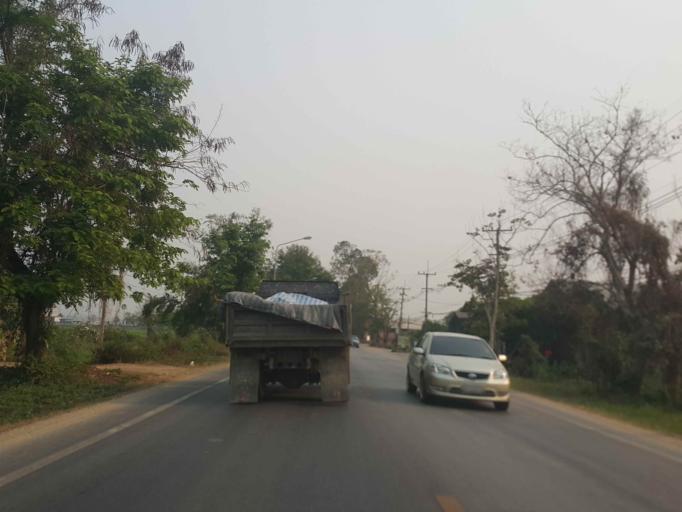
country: TH
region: Chiang Mai
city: Mae Taeng
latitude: 19.0185
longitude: 98.9699
